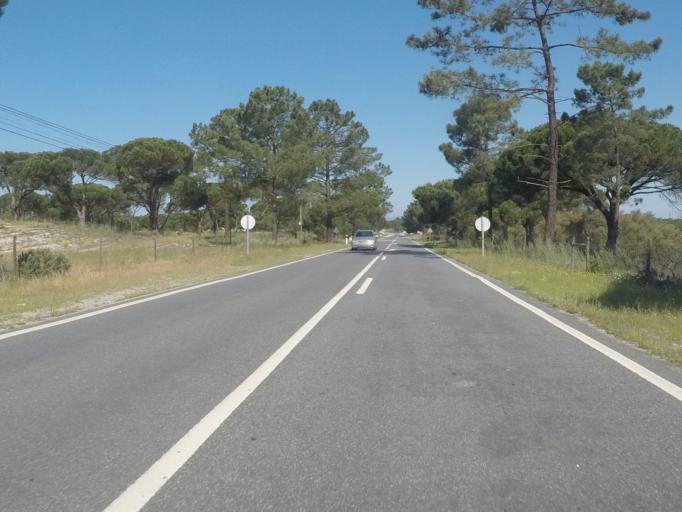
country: PT
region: Setubal
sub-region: Grandola
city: Grandola
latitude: 38.3048
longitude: -8.7371
